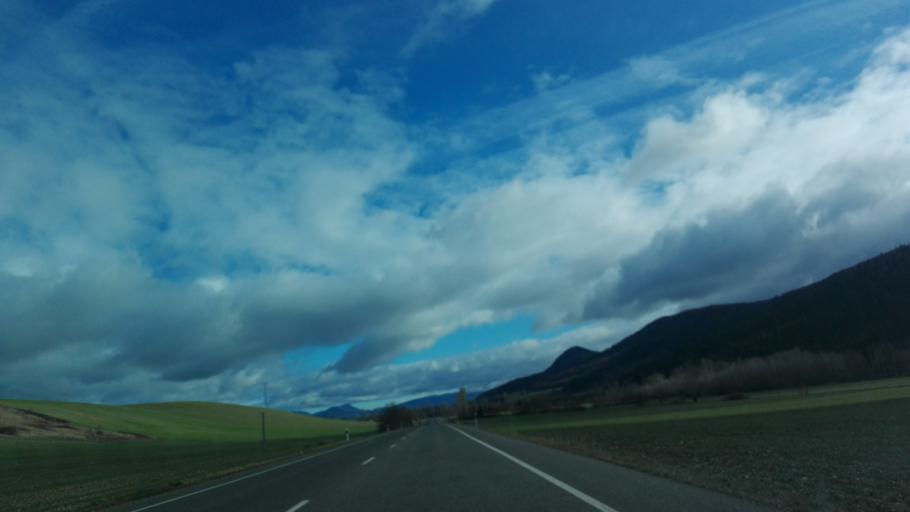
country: ES
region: Navarre
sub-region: Provincia de Navarra
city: Lizoain
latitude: 42.7776
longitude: -1.4486
